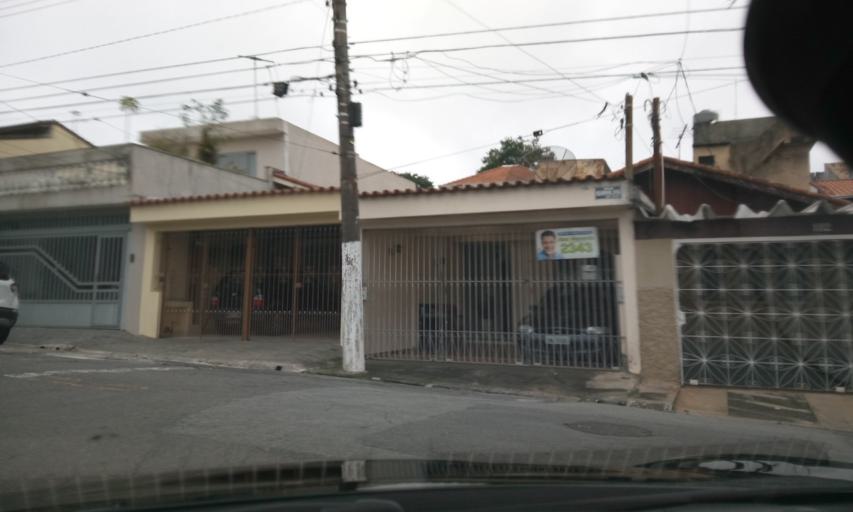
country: BR
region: Sao Paulo
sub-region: Sao Bernardo Do Campo
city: Sao Bernardo do Campo
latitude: -23.6757
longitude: -46.5631
